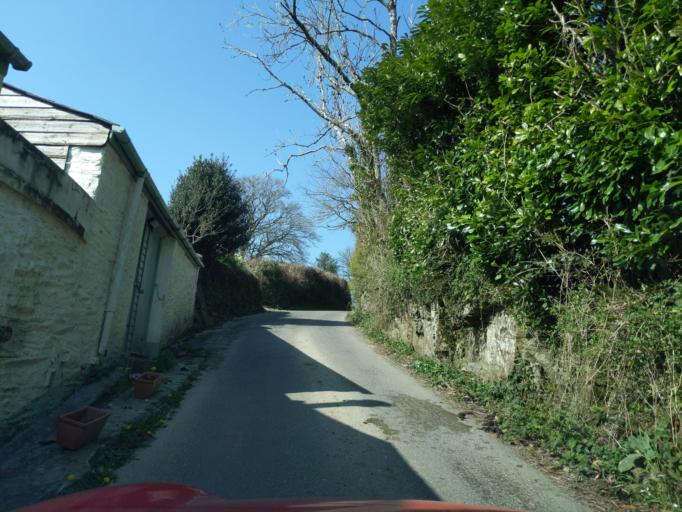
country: GB
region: England
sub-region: Devon
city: Horrabridge
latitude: 50.4767
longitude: -4.1314
